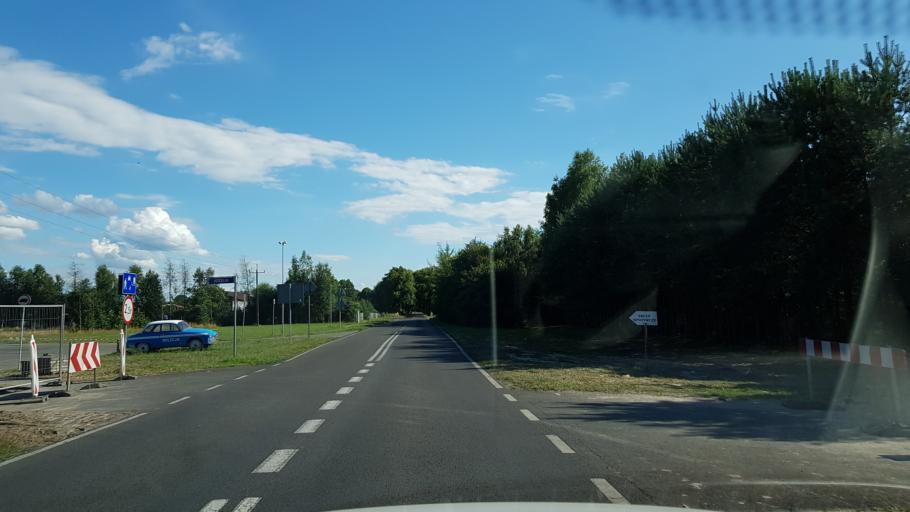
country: PL
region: West Pomeranian Voivodeship
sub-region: Powiat goleniowski
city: Goleniow
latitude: 53.5959
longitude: 14.7401
